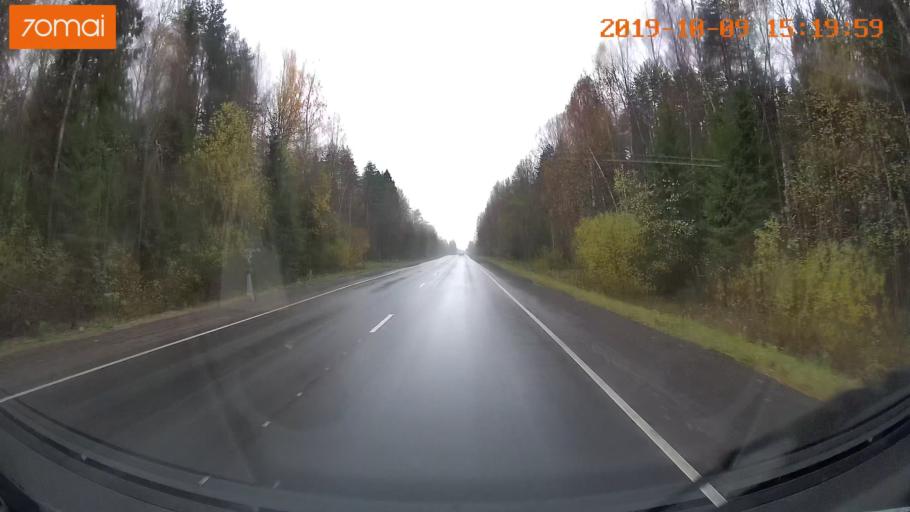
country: RU
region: Kostroma
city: Susanino
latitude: 58.0695
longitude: 41.5463
